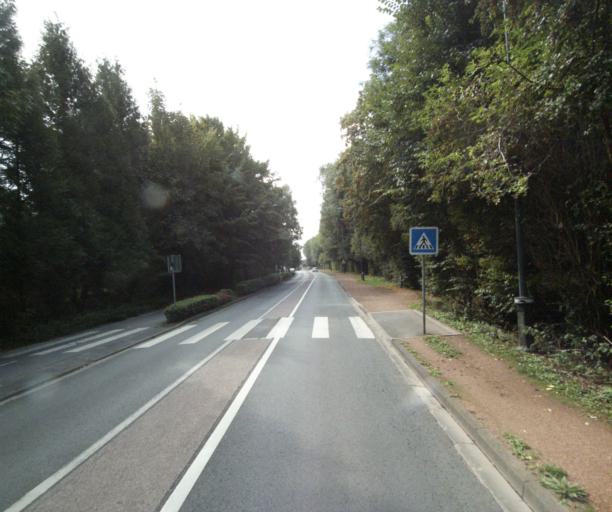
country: FR
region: Nord-Pas-de-Calais
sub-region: Departement du Nord
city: Villeneuve-d'Ascq
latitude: 50.6330
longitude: 3.1551
